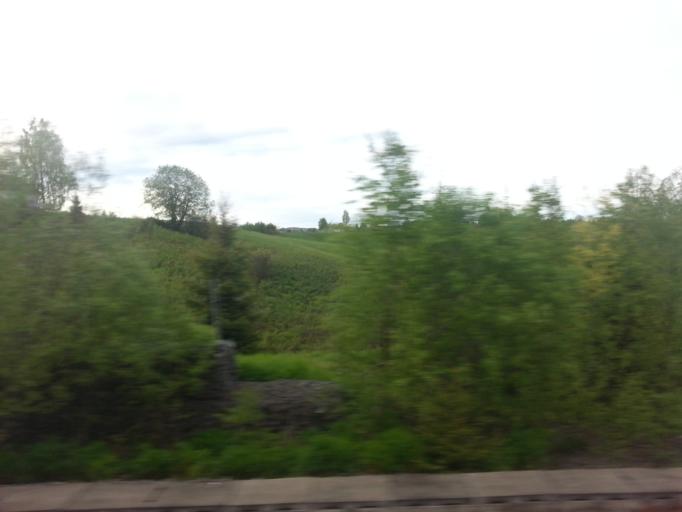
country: NO
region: Akershus
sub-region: Eidsvoll
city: Raholt
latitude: 60.2979
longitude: 11.1907
